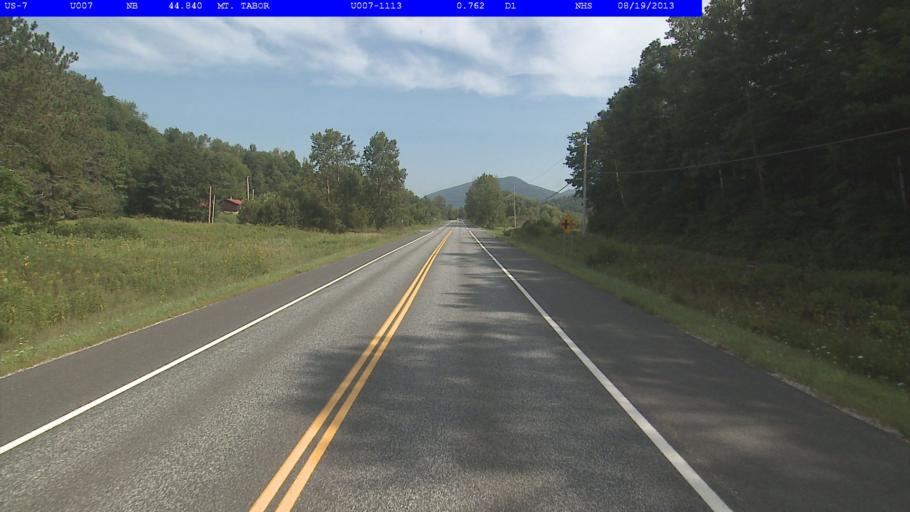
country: US
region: Vermont
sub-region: Bennington County
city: Manchester Center
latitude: 43.3159
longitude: -72.9920
